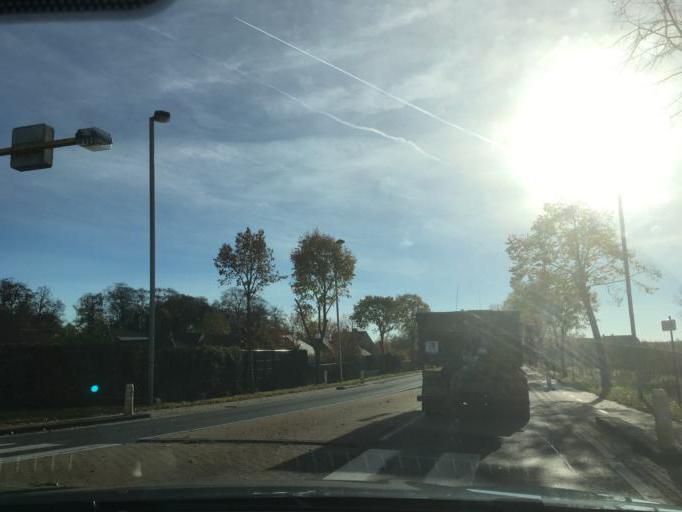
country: BE
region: Flanders
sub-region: Provincie West-Vlaanderen
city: Meulebeke
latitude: 50.9488
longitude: 3.2764
